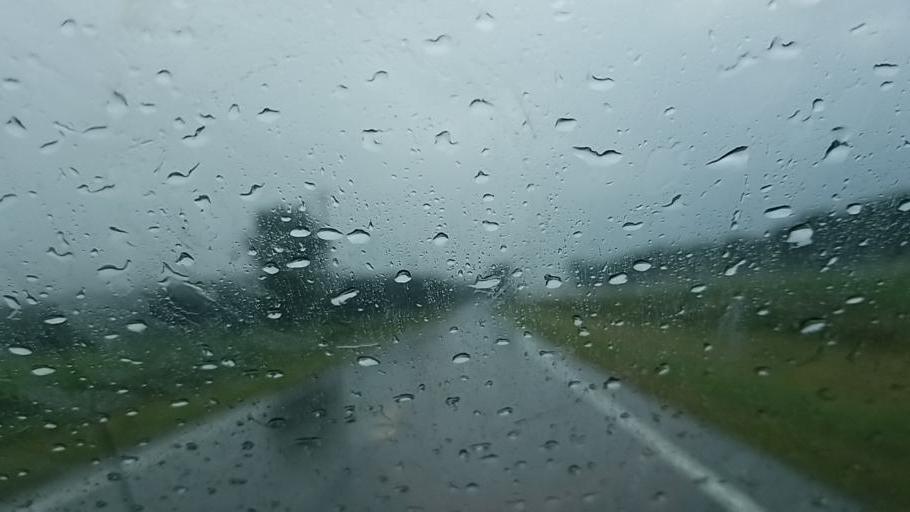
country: US
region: Ohio
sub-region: Champaign County
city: North Lewisburg
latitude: 40.3265
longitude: -83.6307
